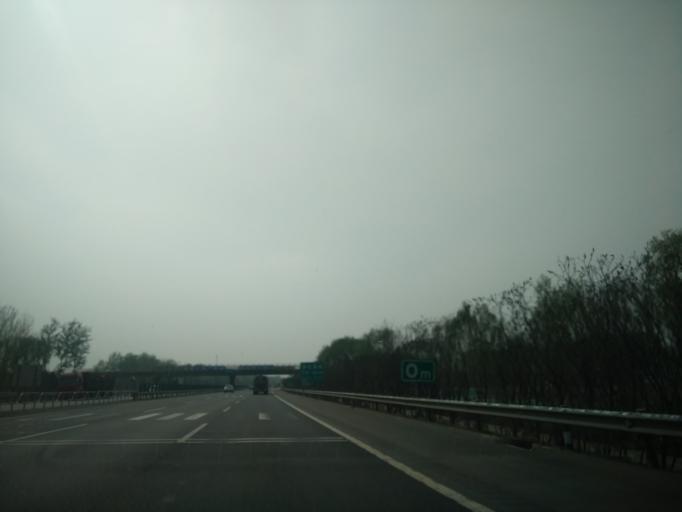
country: CN
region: Beijing
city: Huoxian
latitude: 39.8013
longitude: 116.8152
